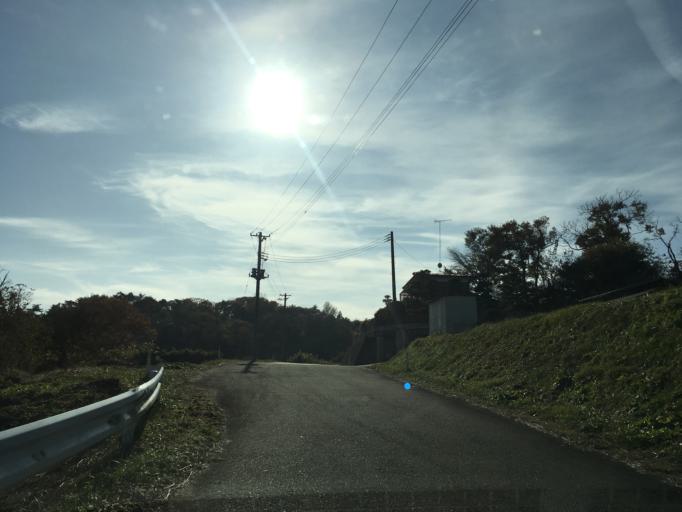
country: JP
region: Iwate
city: Ichinoseki
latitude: 38.7833
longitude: 141.2294
